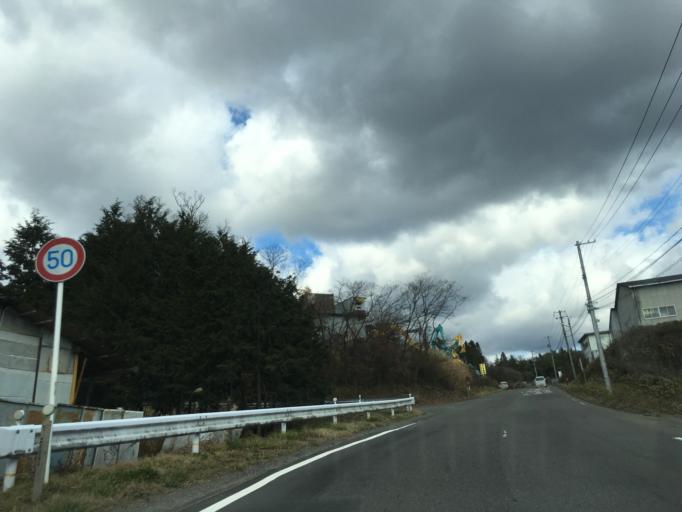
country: JP
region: Fukushima
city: Sukagawa
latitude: 37.3316
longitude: 140.4400
